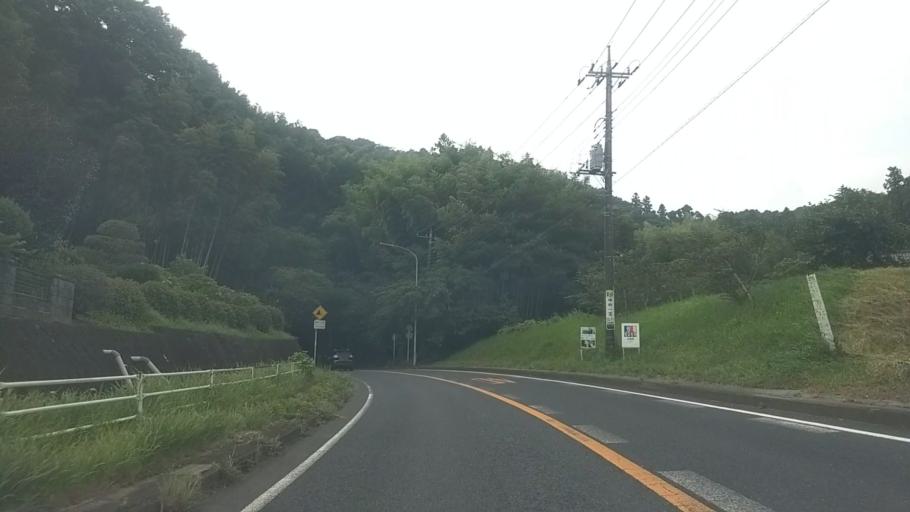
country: JP
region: Chiba
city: Kimitsu
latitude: 35.3138
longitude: 139.9608
